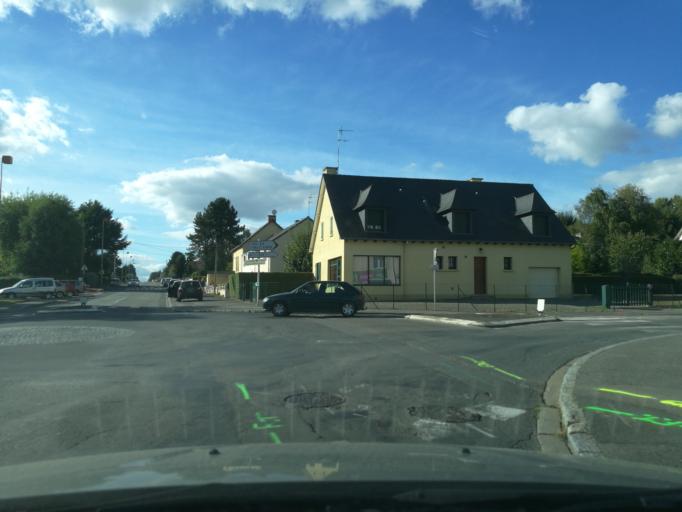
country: FR
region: Brittany
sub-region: Departement d'Ille-et-Vilaine
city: Montauban-de-Bretagne
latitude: 48.2018
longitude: -2.0505
